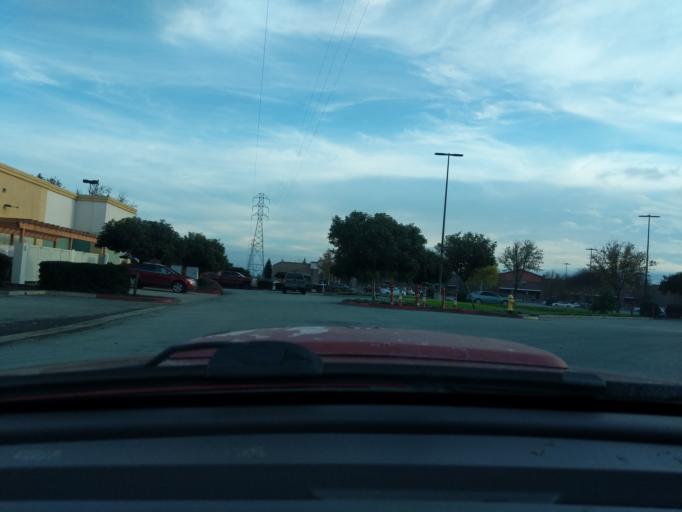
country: US
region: California
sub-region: Santa Clara County
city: Gilroy
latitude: 37.0021
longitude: -121.5526
